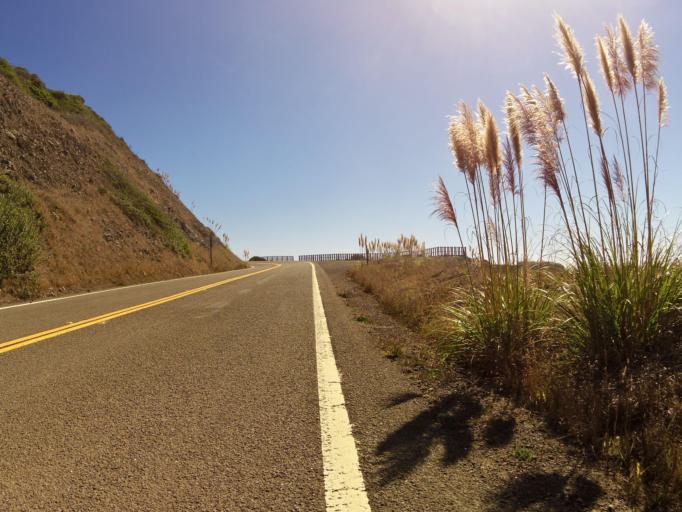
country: US
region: California
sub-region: Mendocino County
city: Fort Bragg
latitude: 39.7011
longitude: -123.8033
